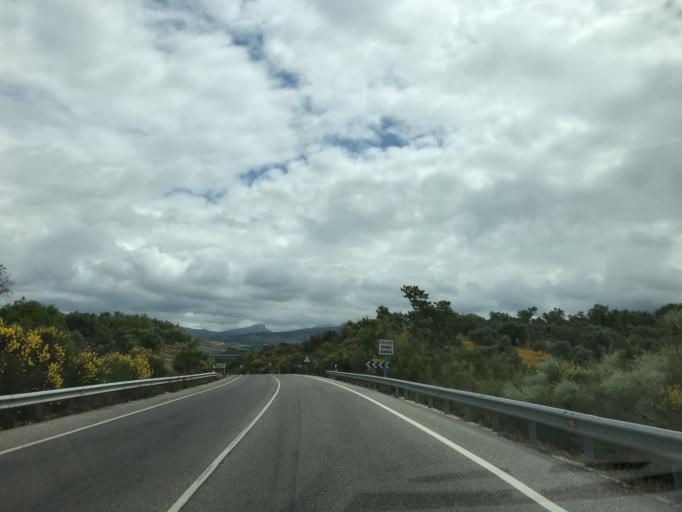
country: ES
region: Andalusia
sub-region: Provincia de Malaga
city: Ronda
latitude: 36.7230
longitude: -5.1506
